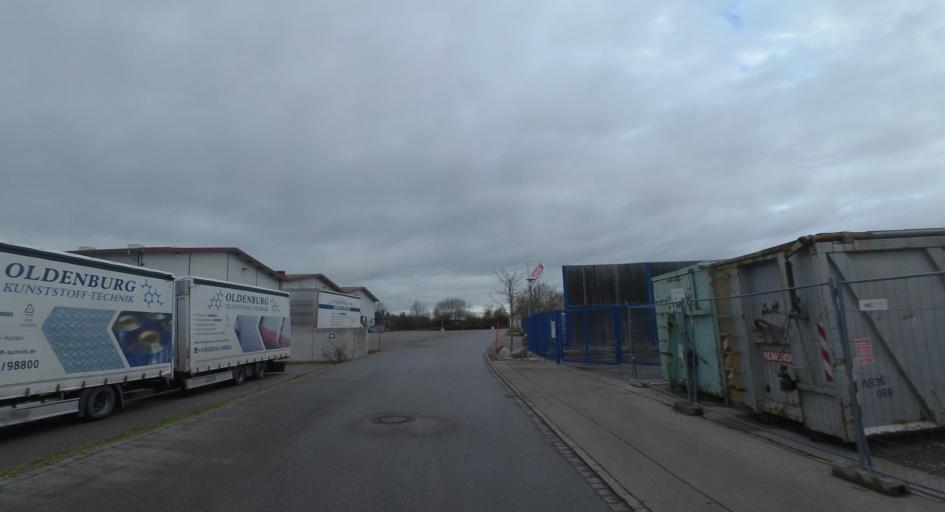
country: DE
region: Bavaria
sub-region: Upper Bavaria
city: Chieming
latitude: 47.9105
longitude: 12.5339
